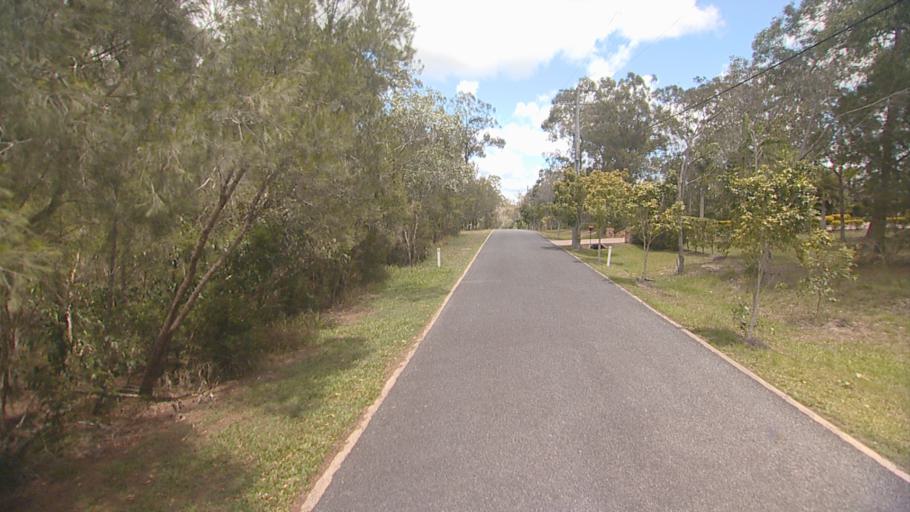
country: AU
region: Queensland
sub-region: Logan
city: Beenleigh
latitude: -27.6585
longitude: 153.2303
